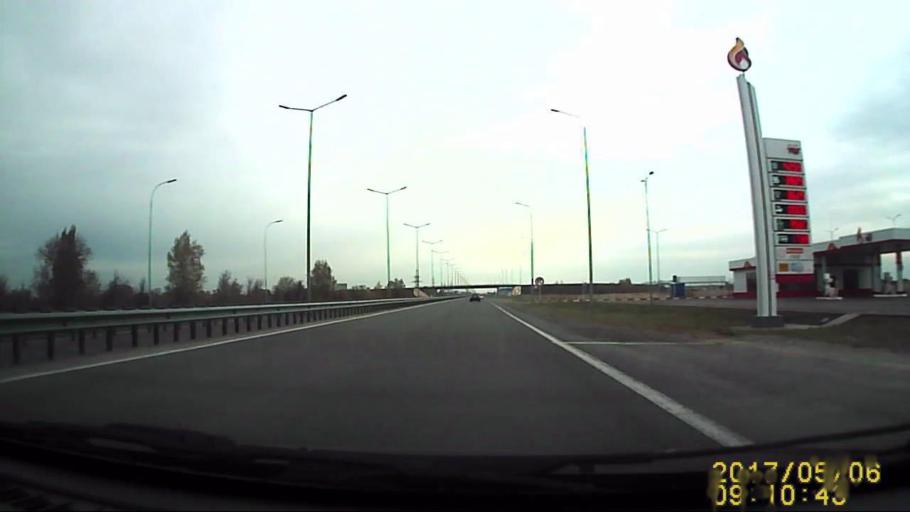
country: RU
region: Ulyanovsk
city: Mirnyy
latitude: 54.3484
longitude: 48.6555
